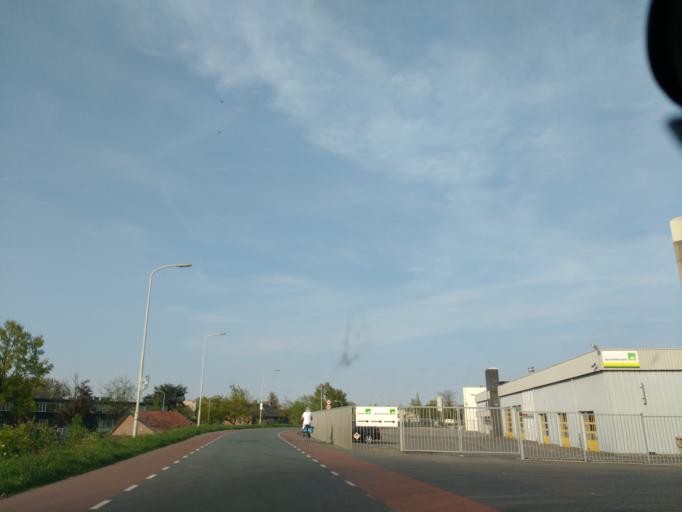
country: NL
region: Gelderland
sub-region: Gemeente Wageningen
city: Wageningen
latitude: 51.9608
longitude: 5.6525
